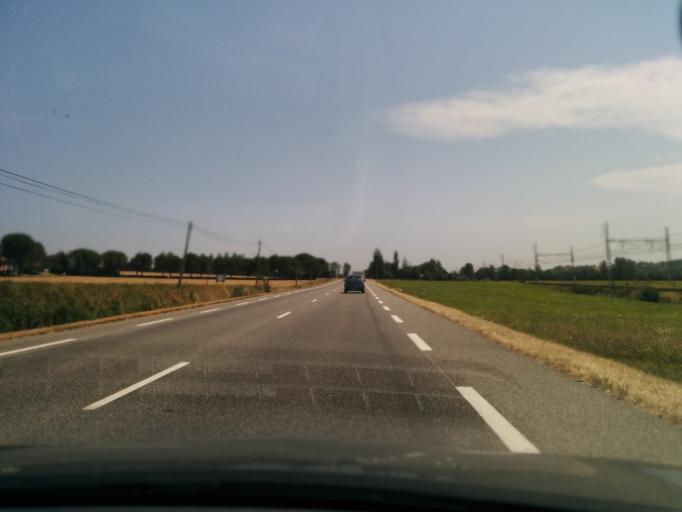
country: FR
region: Midi-Pyrenees
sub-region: Departement de la Haute-Garonne
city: Villefranche-de-Lauragais
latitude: 43.3778
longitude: 1.7530
